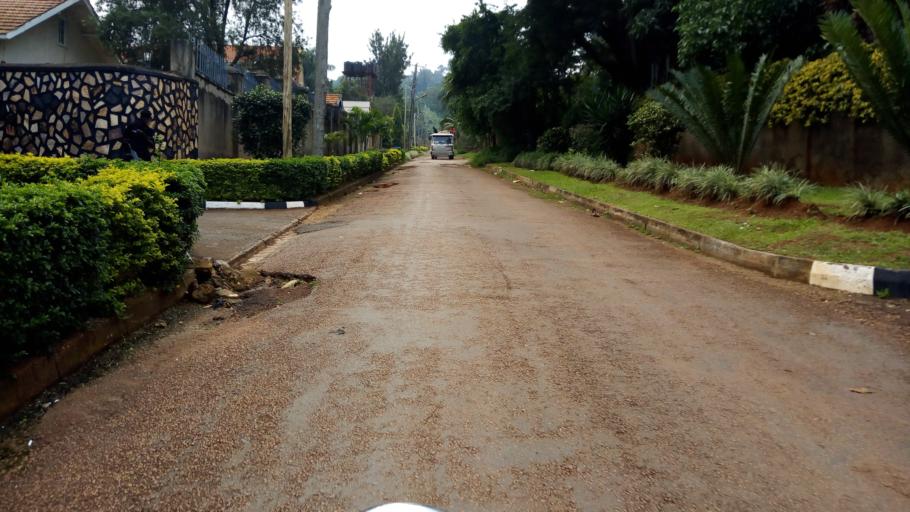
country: UG
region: Central Region
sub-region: Wakiso District
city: Kireka
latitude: 0.3195
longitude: 32.6292
